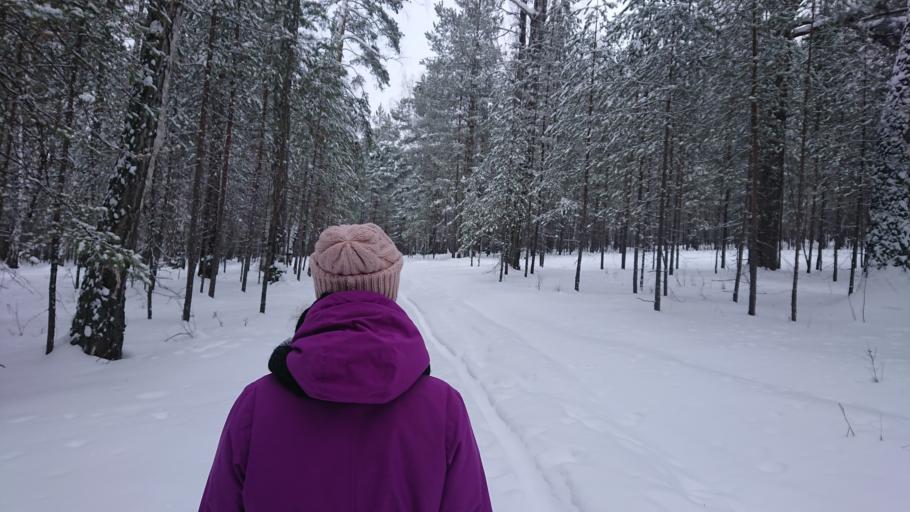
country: RU
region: Sverdlovsk
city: Degtyarsk
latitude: 56.6917
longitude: 60.0659
